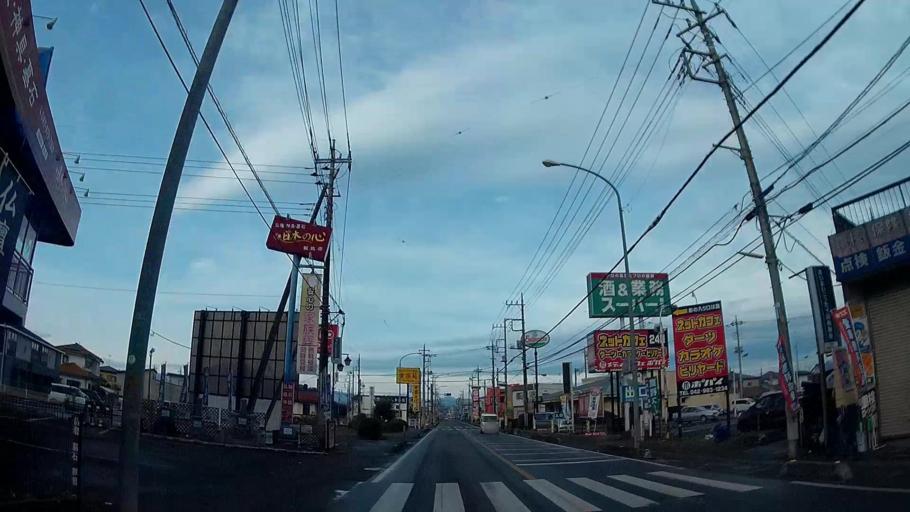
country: JP
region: Saitama
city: Hanno
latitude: 35.8459
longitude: 139.3399
